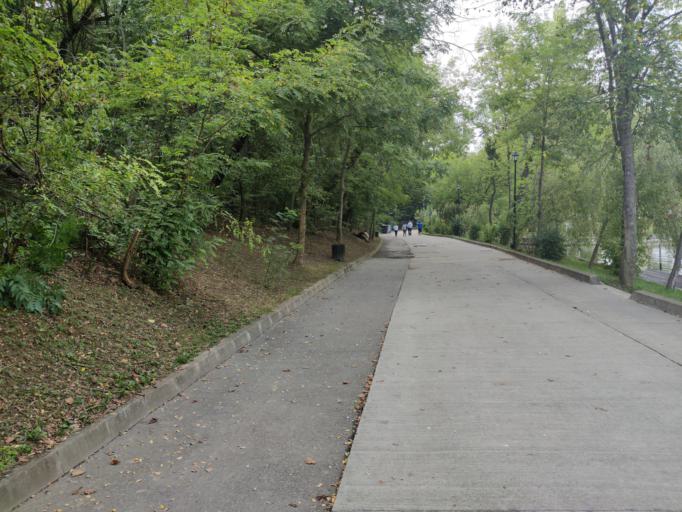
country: RO
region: Iasi
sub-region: Municipiul Iasi
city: Iasi
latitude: 47.1783
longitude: 27.6063
